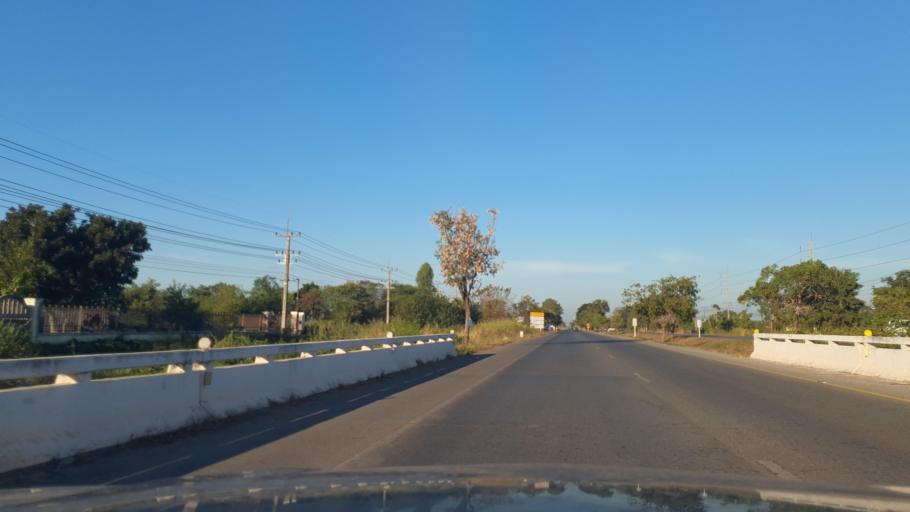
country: TH
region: Phitsanulok
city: Phitsanulok
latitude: 16.8641
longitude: 100.2861
